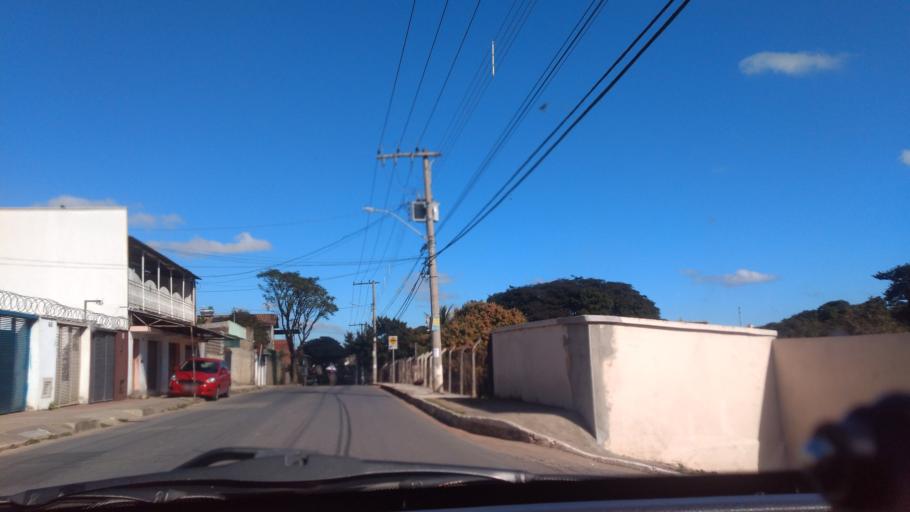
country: BR
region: Minas Gerais
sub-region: Santa Luzia
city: Santa Luzia
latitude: -19.8108
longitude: -43.9430
